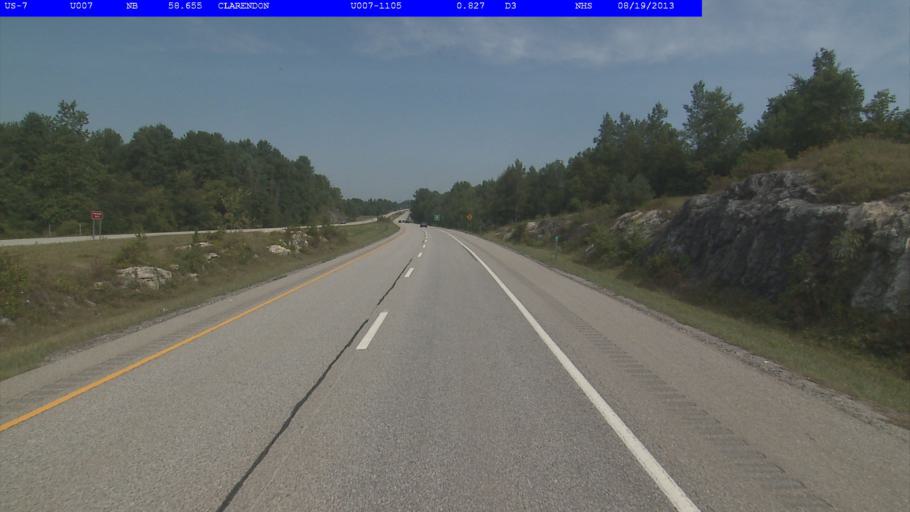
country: US
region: Vermont
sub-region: Rutland County
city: Rutland
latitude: 43.5061
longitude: -72.9669
